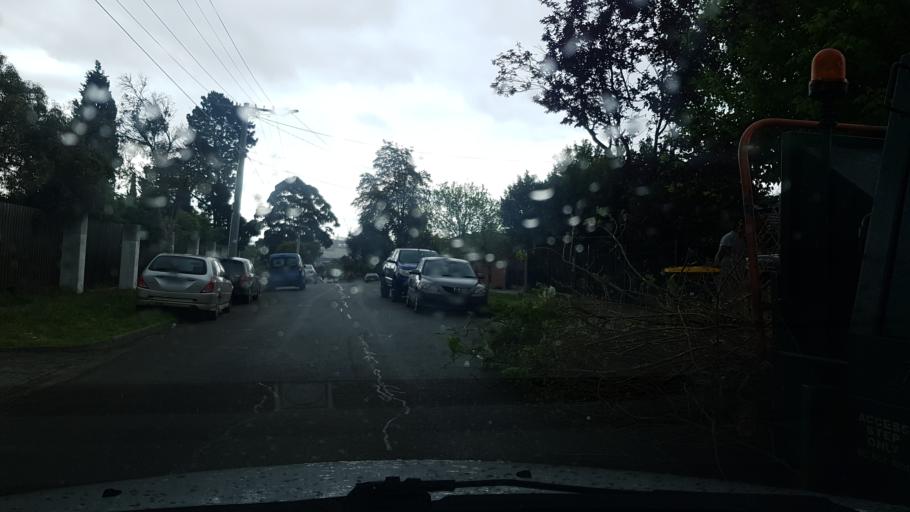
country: AU
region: Victoria
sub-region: Greater Dandenong
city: Springvale
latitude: -37.9287
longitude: 145.1520
